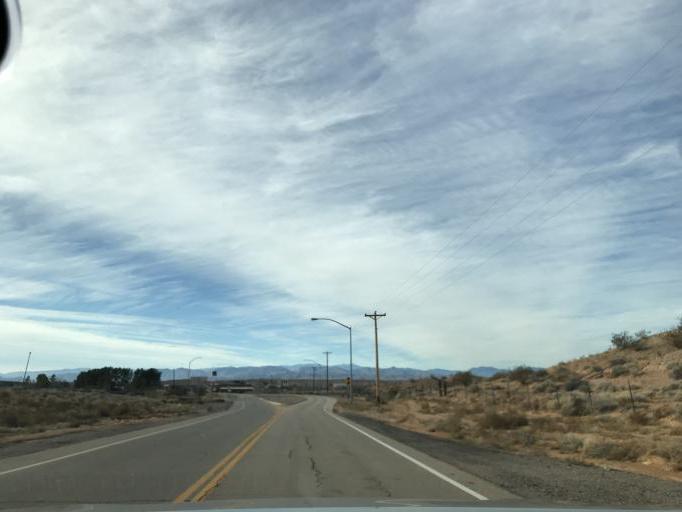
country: US
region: Nevada
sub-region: Clark County
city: Moapa Town
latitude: 36.6664
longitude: -114.5635
